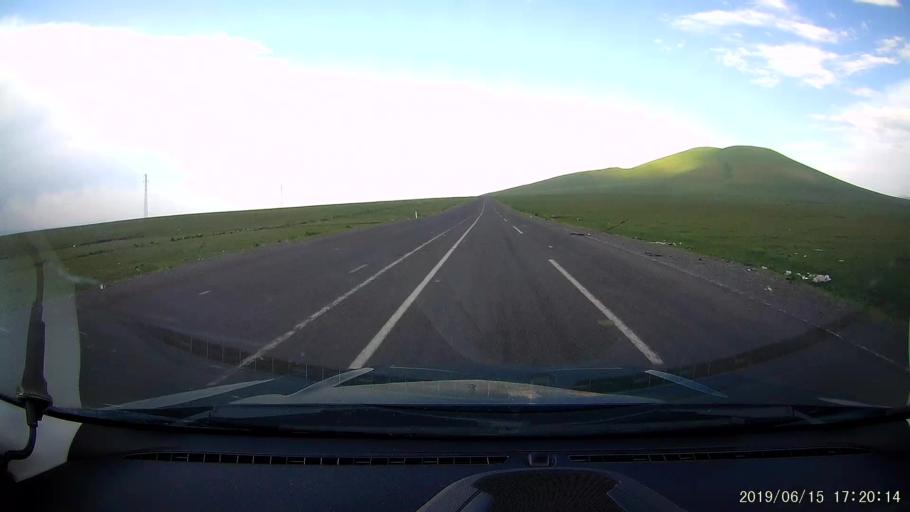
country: TR
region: Kars
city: Kars
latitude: 40.6161
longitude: 43.2963
